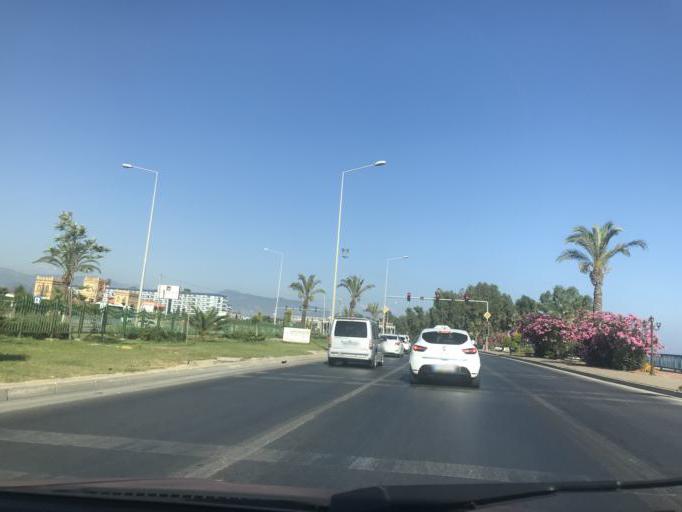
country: TR
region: Antalya
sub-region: Alanya
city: Tuerkler
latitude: 36.5960
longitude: 31.8115
